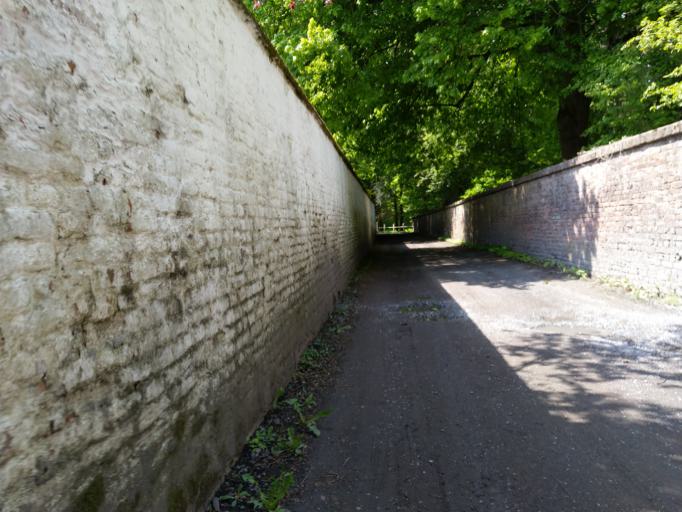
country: BE
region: Wallonia
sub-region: Province du Hainaut
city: Mons
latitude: 50.4593
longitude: 4.0313
